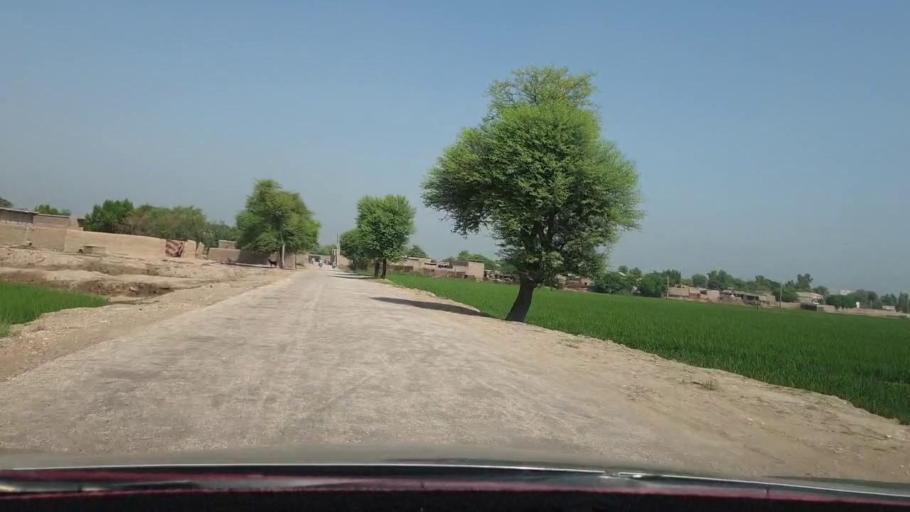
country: PK
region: Sindh
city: Warah
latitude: 27.4799
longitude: 67.8304
